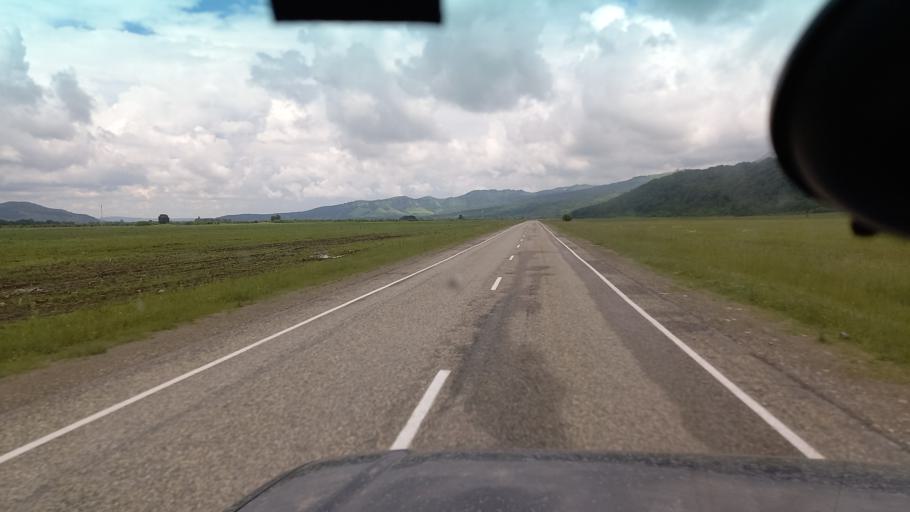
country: RU
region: Krasnodarskiy
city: Psebay
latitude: 44.0938
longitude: 40.8062
